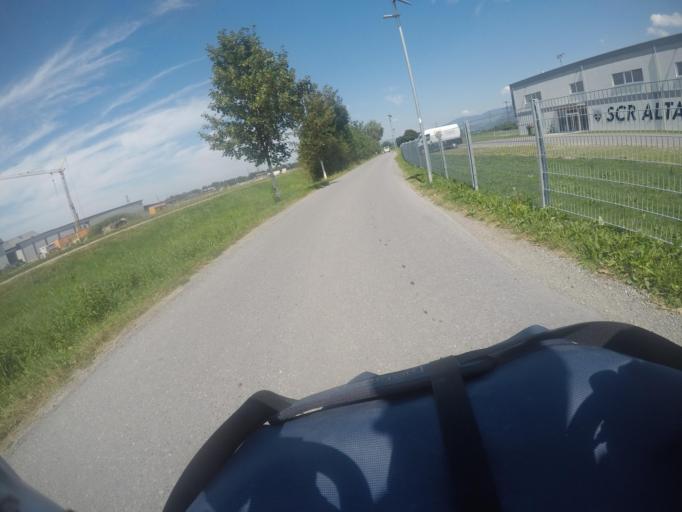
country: AT
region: Vorarlberg
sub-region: Politischer Bezirk Feldkirch
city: Altach
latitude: 47.3562
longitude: 9.6360
